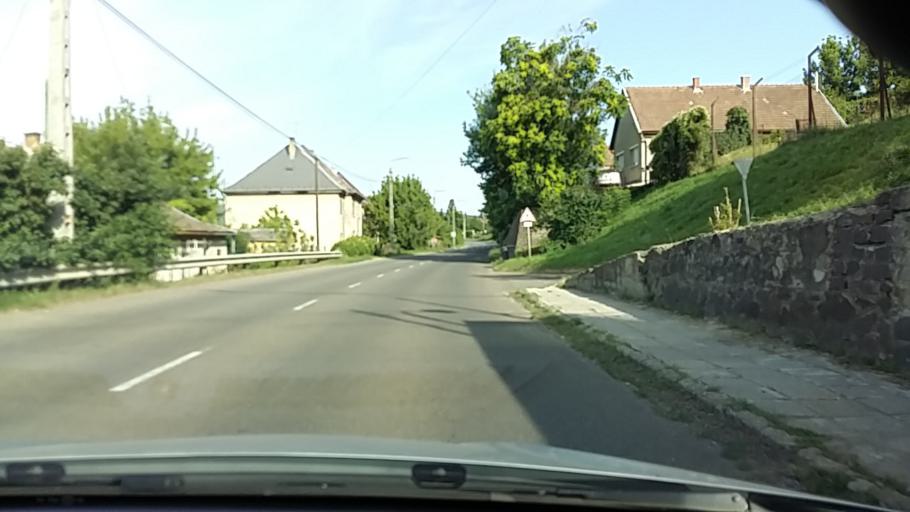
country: HU
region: Pest
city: Szob
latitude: 47.8207
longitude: 18.8651
